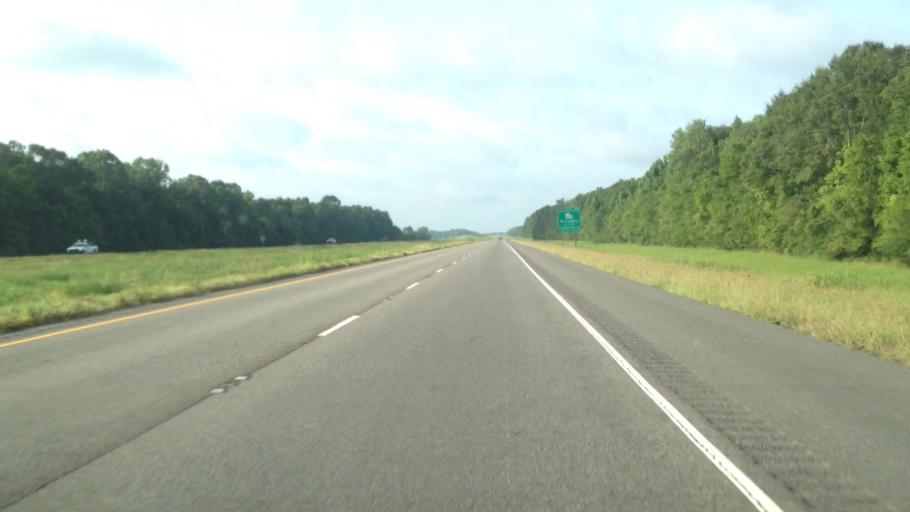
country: US
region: Louisiana
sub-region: Avoyelles Parish
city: Bunkie
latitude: 30.8805
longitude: -92.2277
